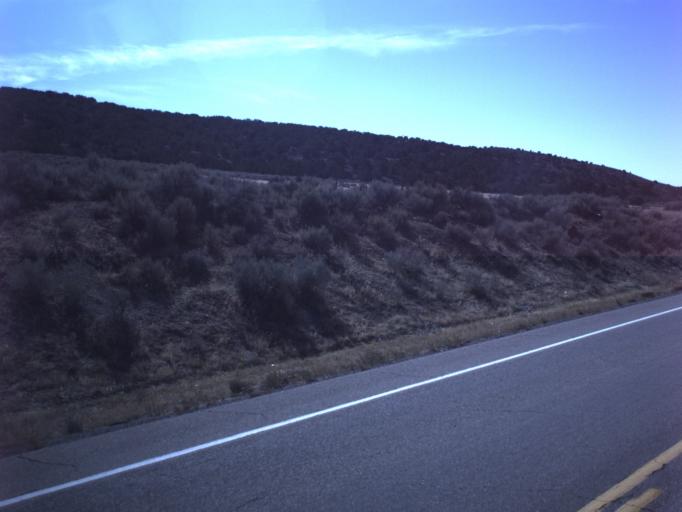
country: US
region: Utah
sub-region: Sanpete County
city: Gunnison
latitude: 39.4147
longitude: -111.9241
